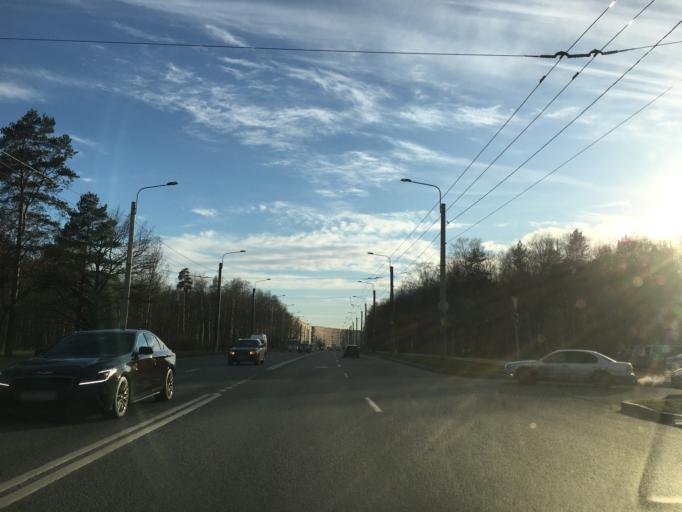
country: RU
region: St.-Petersburg
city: Dachnoye
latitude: 59.8375
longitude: 30.2308
